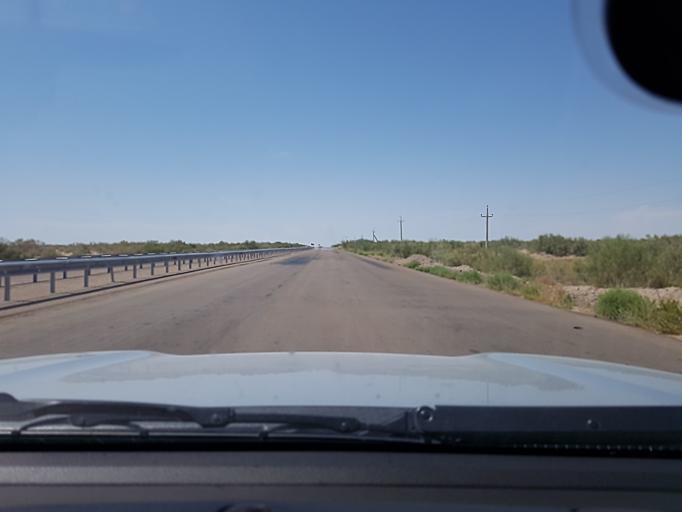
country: TM
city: Akdepe
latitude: 41.7368
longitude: 59.0237
